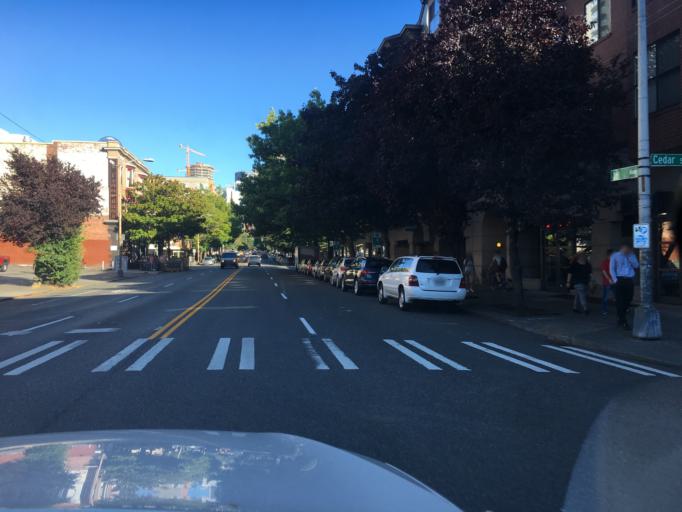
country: US
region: Washington
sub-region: King County
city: Seattle
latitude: 47.6159
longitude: -122.3507
